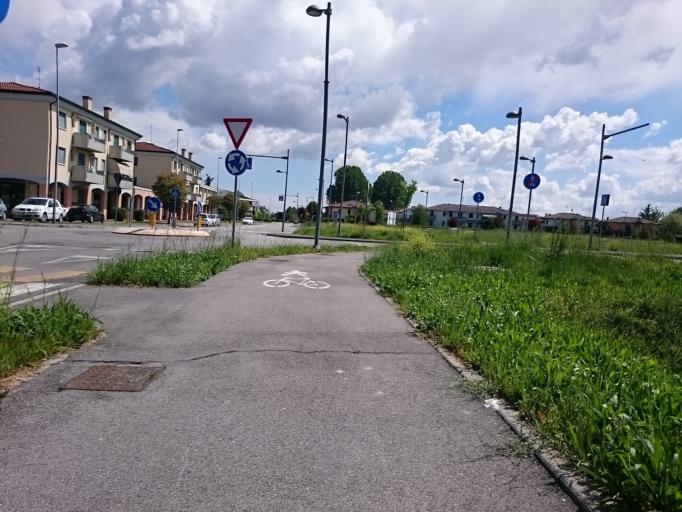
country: IT
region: Veneto
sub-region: Provincia di Padova
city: Casalserugo
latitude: 45.3230
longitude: 11.9080
